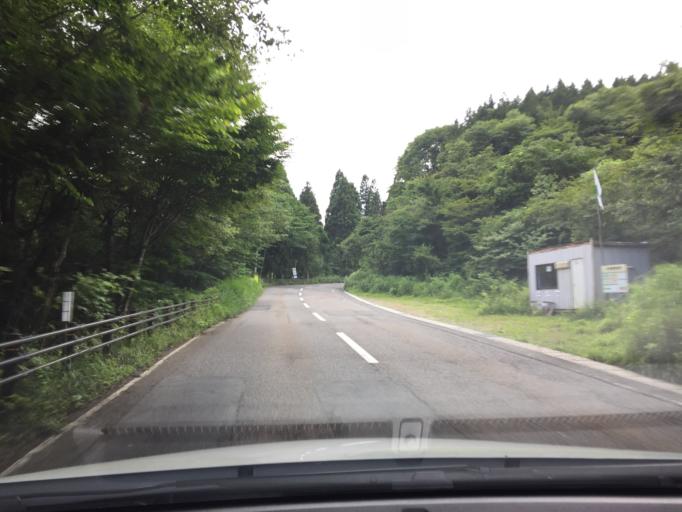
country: JP
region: Fukushima
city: Sukagawa
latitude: 37.2653
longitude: 140.1147
